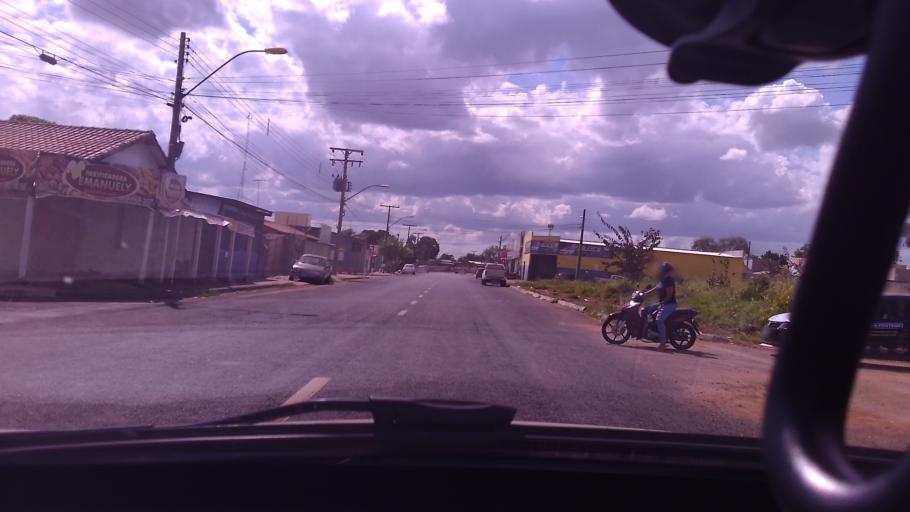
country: BR
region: Goias
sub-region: Mineiros
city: Mineiros
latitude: -17.5406
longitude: -52.5422
